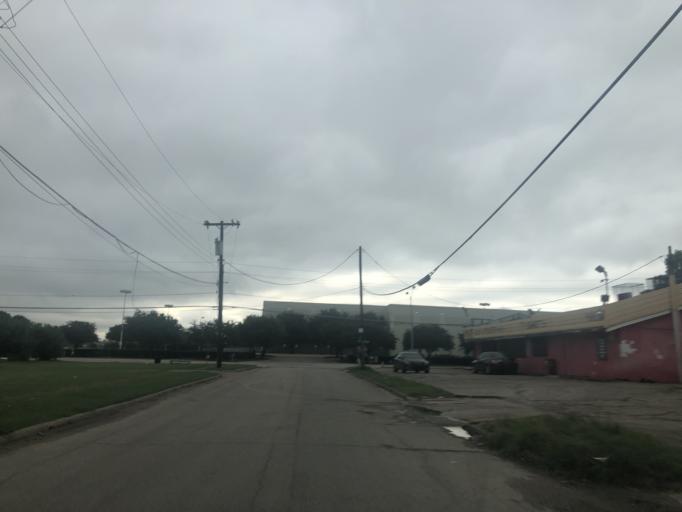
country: US
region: Texas
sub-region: Dallas County
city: Cockrell Hill
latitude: 32.7816
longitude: -96.8747
